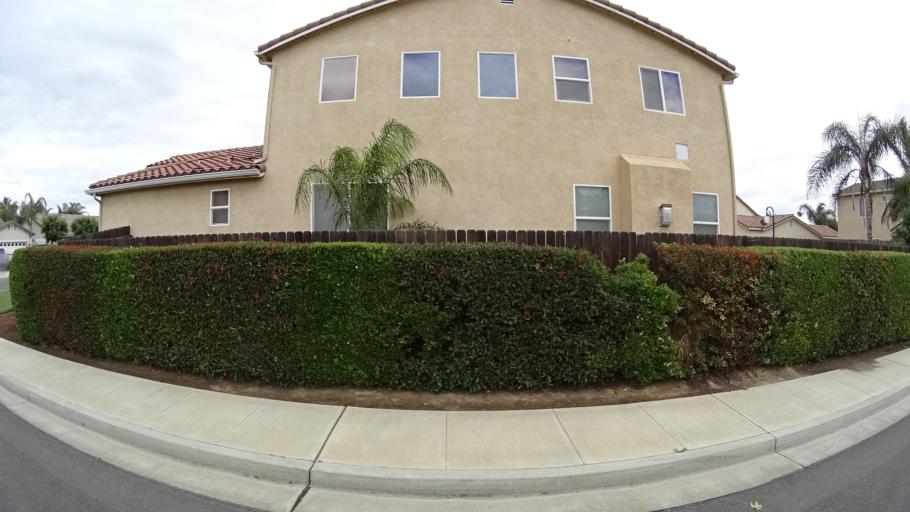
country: US
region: California
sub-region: Kings County
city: Armona
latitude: 36.3315
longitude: -119.6836
